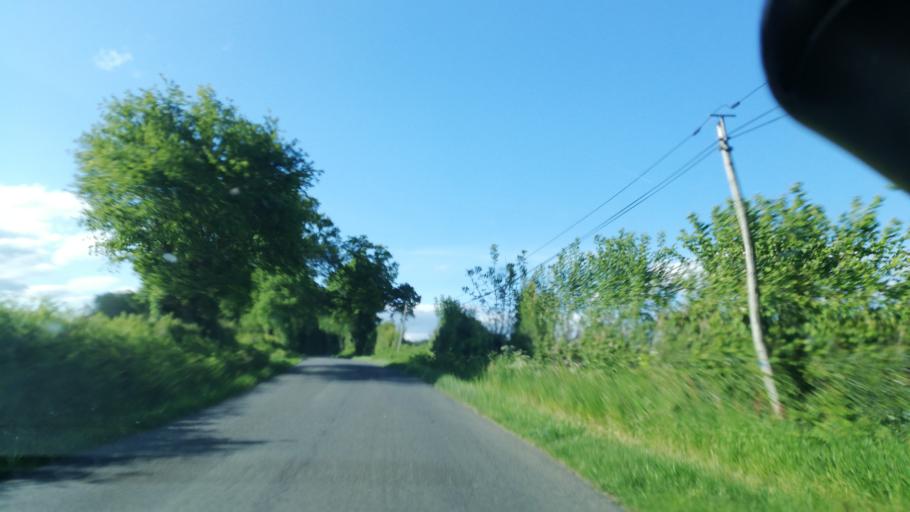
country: FR
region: Poitou-Charentes
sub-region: Departement des Deux-Sevres
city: Boisme
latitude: 46.7831
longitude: -0.4311
